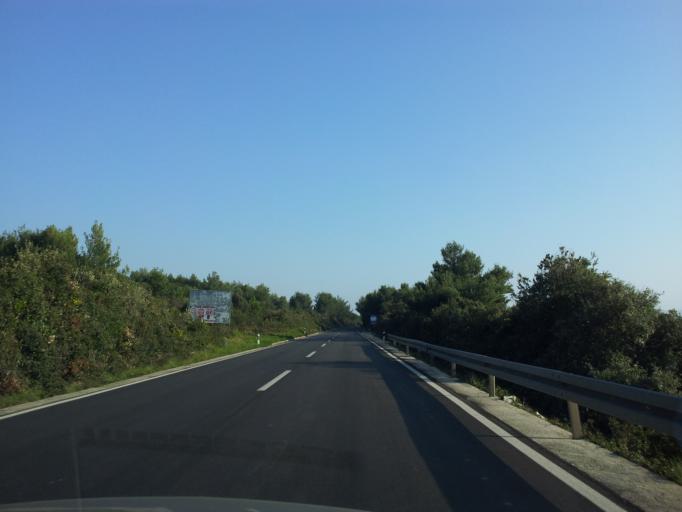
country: HR
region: Zadarska
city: Sukosan
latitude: 44.0142
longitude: 15.3612
